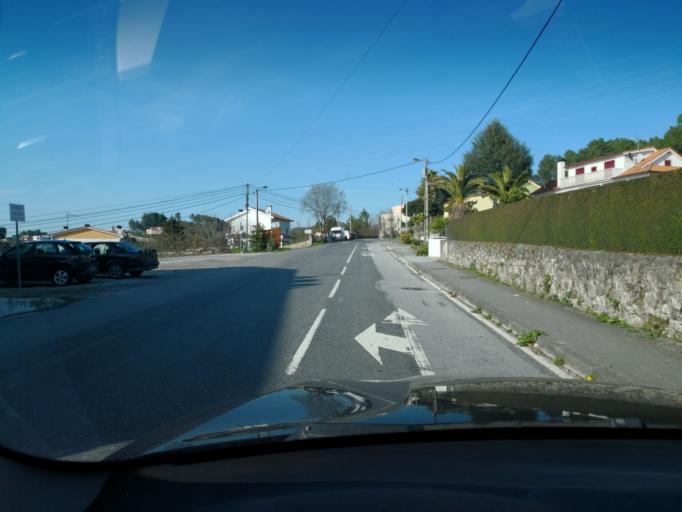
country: PT
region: Vila Real
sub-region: Vila Real
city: Vila Real
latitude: 41.3212
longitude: -7.6944
